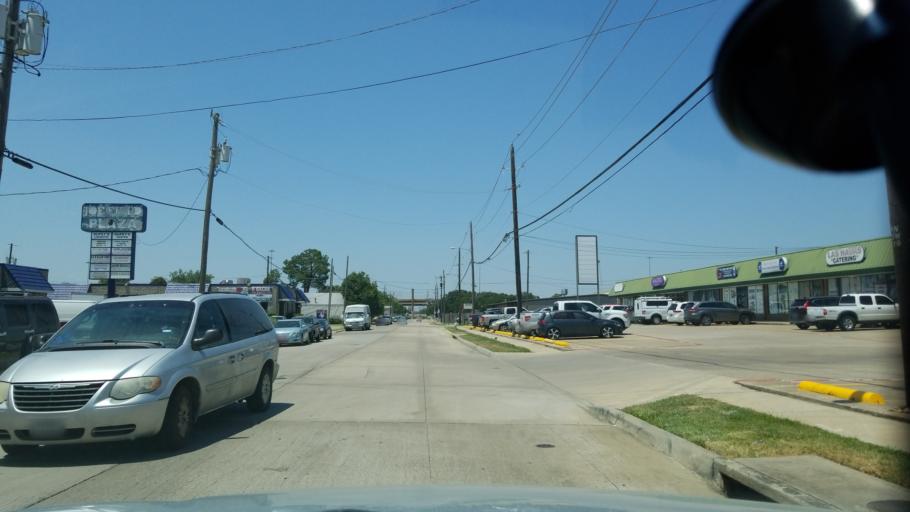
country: US
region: Texas
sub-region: Dallas County
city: Farmers Branch
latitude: 32.8929
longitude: -96.8922
